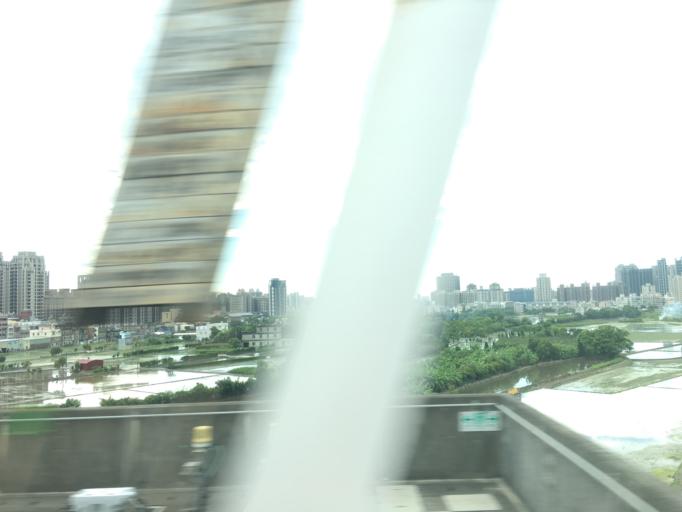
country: TW
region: Taiwan
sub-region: Hsinchu
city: Zhubei
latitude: 24.8149
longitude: 121.0419
